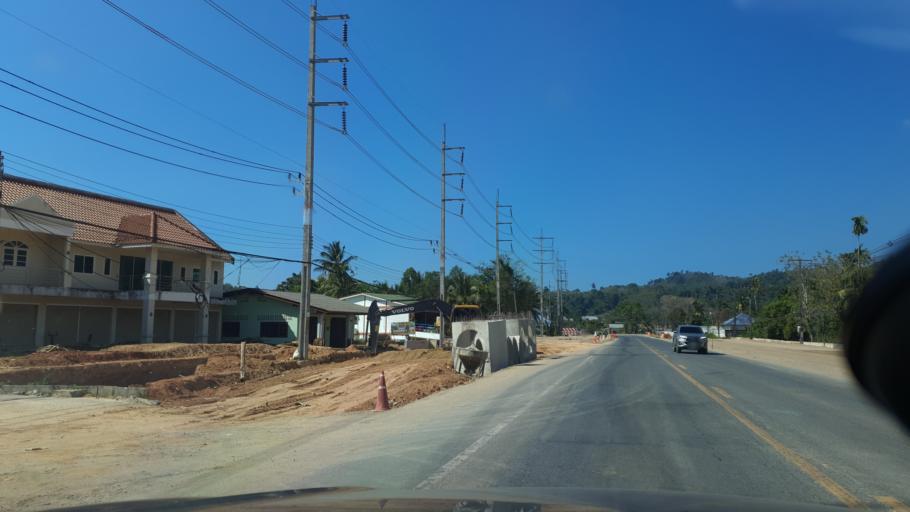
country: TH
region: Phangnga
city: Ban Khao Lak
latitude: 8.5978
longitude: 98.2555
